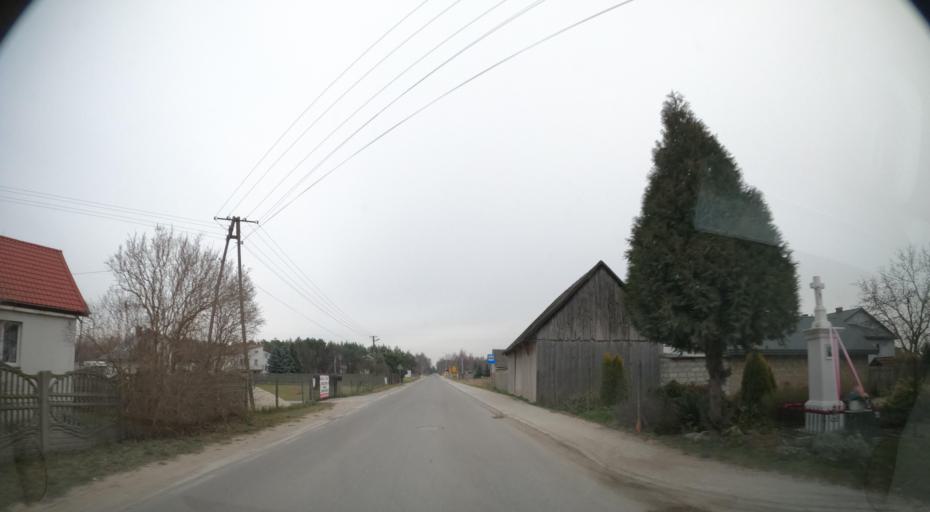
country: PL
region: Masovian Voivodeship
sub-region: Powiat radomski
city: Jastrzebia
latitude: 51.4891
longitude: 21.1877
